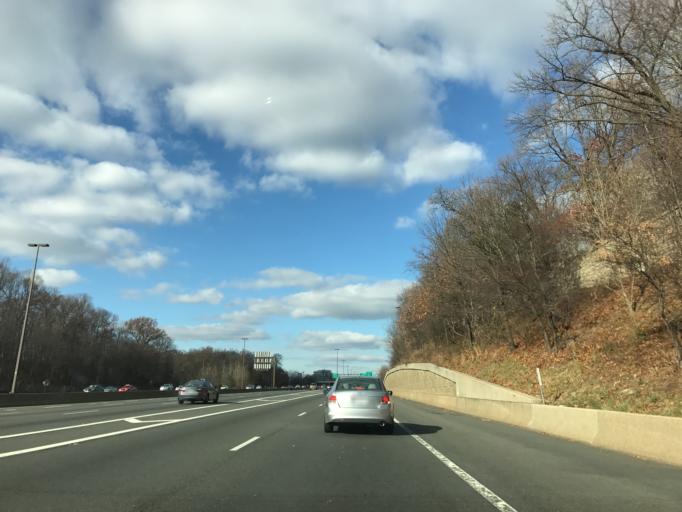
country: US
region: Maryland
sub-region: Montgomery County
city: North Bethesda
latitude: 39.0501
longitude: -77.1516
